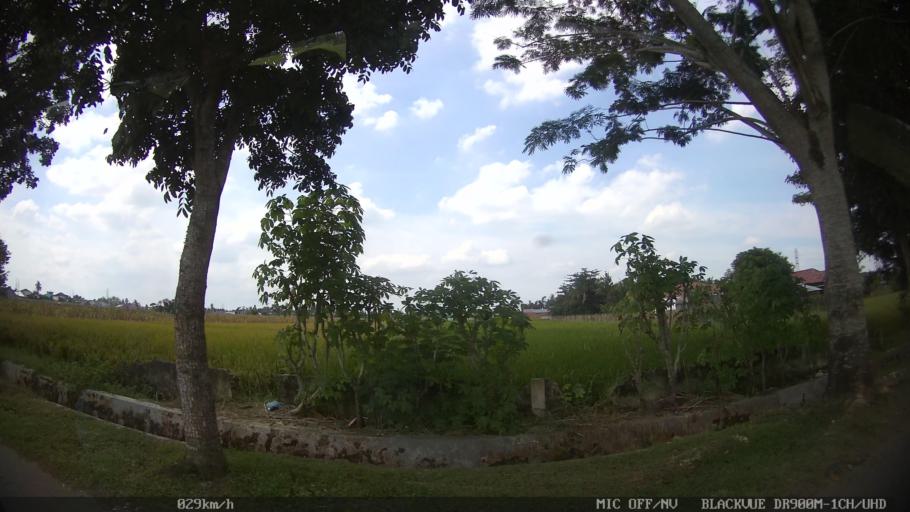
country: ID
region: North Sumatra
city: Binjai
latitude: 3.6209
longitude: 98.5159
